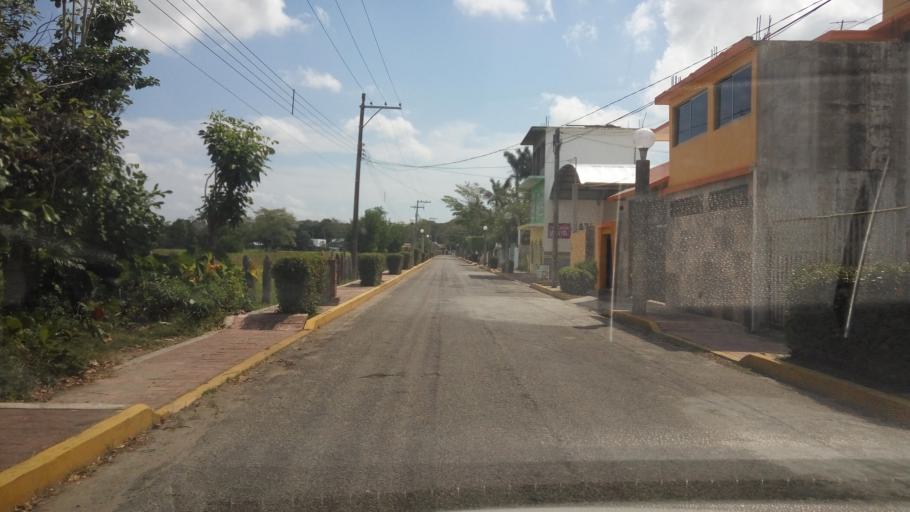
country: MX
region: Tabasco
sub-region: Comalcalco
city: Oriente 1ra. Seccion (Santo Domingo)
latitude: 18.2807
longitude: -93.2090
